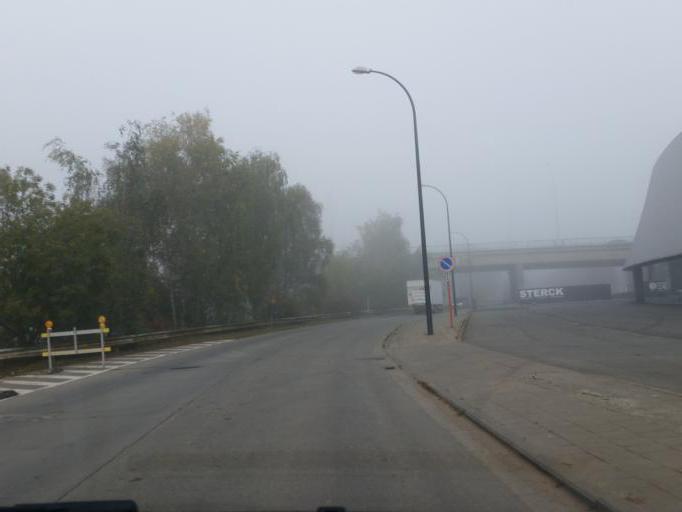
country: BE
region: Flanders
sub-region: Provincie Oost-Vlaanderen
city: Aalst
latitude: 50.9483
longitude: 4.0373
